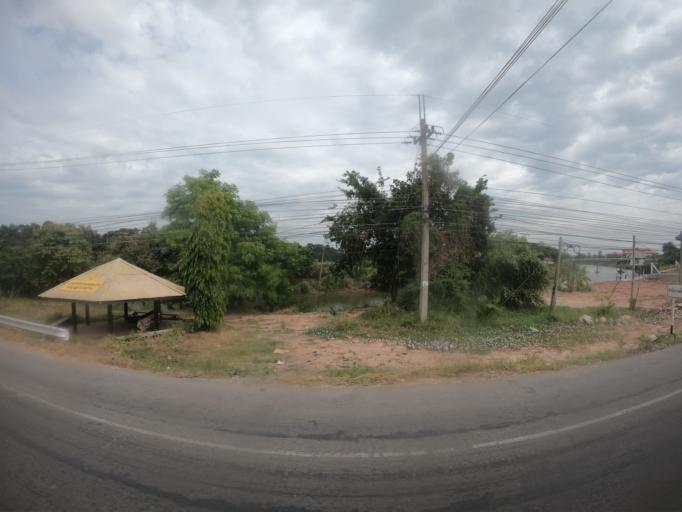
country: TH
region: Maha Sarakham
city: Maha Sarakham
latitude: 16.2176
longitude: 103.2766
